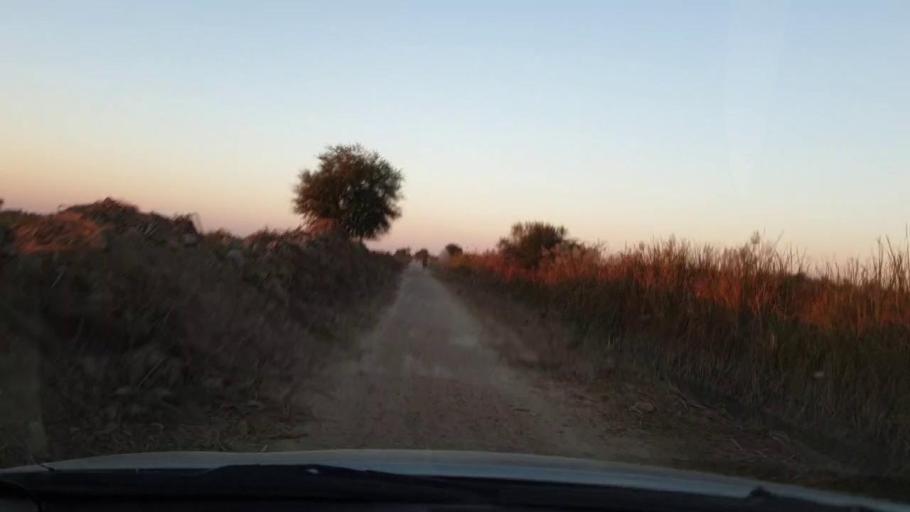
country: PK
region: Sindh
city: Jhol
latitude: 25.9020
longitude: 68.8863
